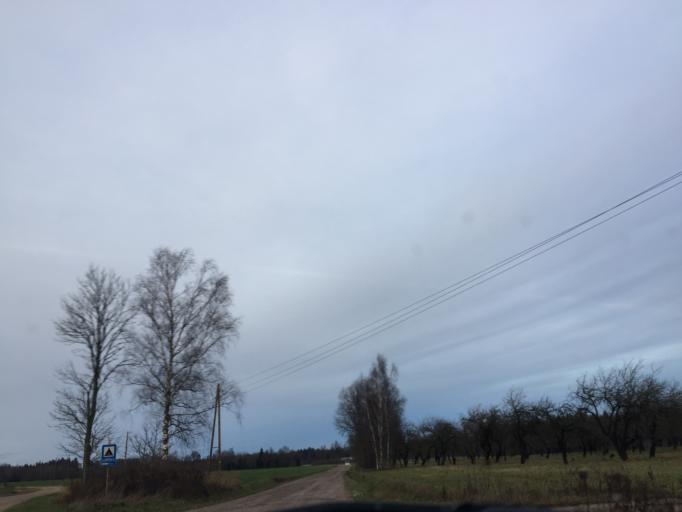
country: LV
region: Limbazu Rajons
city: Limbazi
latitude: 57.5293
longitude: 24.8020
